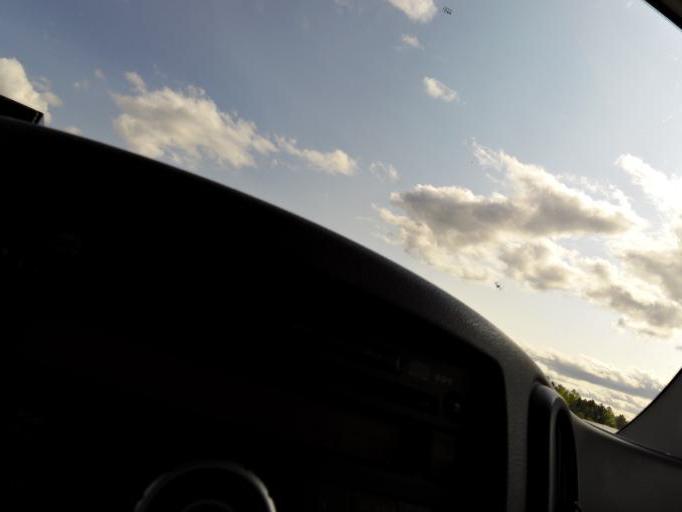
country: US
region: West Virginia
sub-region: Raleigh County
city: Shady Spring
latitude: 37.5546
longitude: -81.1134
